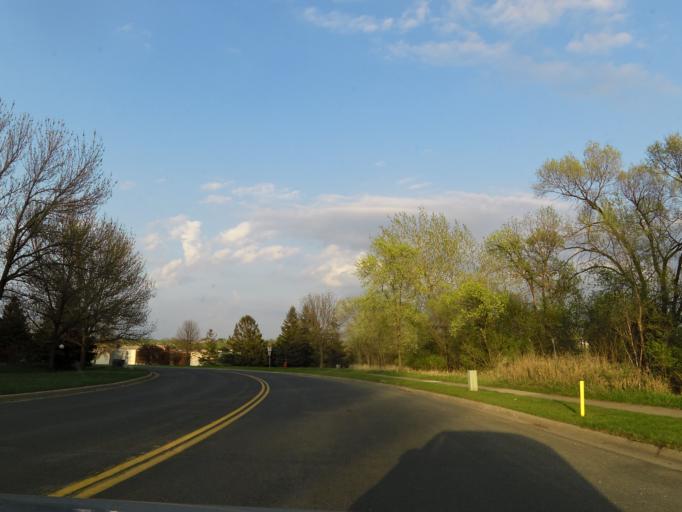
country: US
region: Minnesota
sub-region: Dakota County
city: Eagan
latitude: 44.8192
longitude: -93.2138
